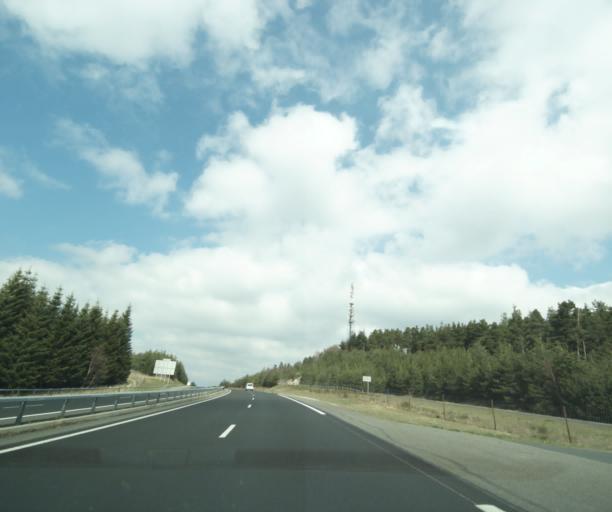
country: FR
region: Languedoc-Roussillon
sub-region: Departement de la Lozere
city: Le Malzieu-Ville
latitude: 44.8563
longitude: 3.2580
